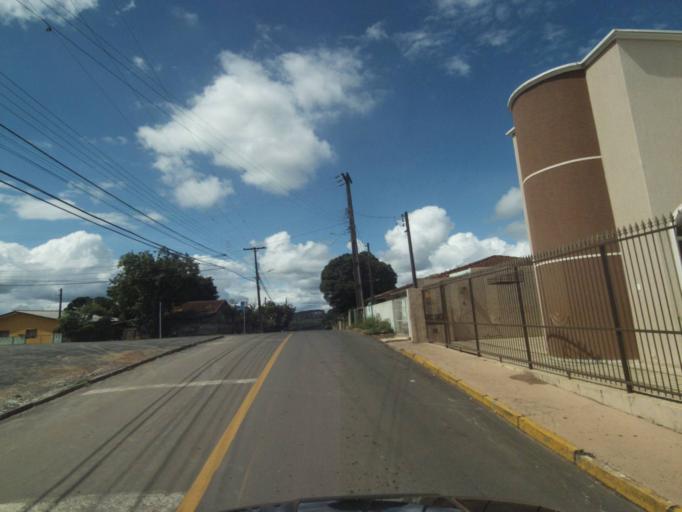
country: BR
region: Parana
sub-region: Telemaco Borba
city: Telemaco Borba
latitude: -24.3168
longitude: -50.6299
